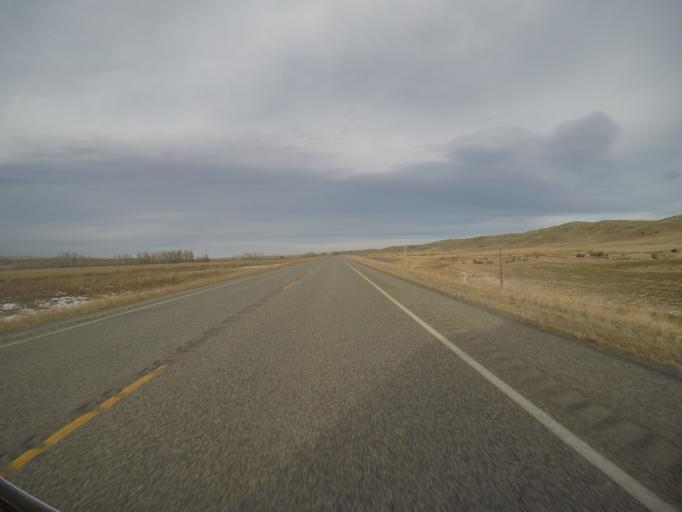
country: US
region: Montana
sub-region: Stillwater County
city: Absarokee
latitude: 45.4461
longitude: -109.4476
